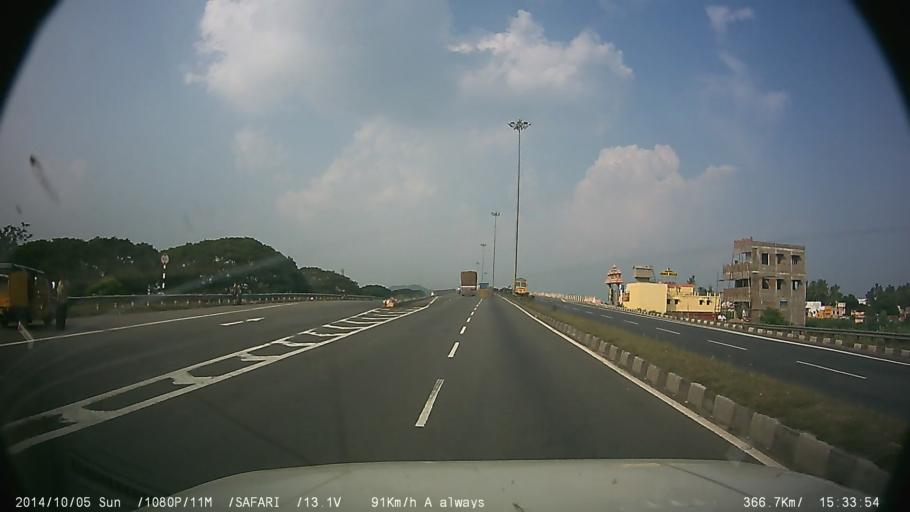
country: IN
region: Tamil Nadu
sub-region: Kancheepuram
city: Chengalpattu
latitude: 12.6973
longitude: 79.9671
